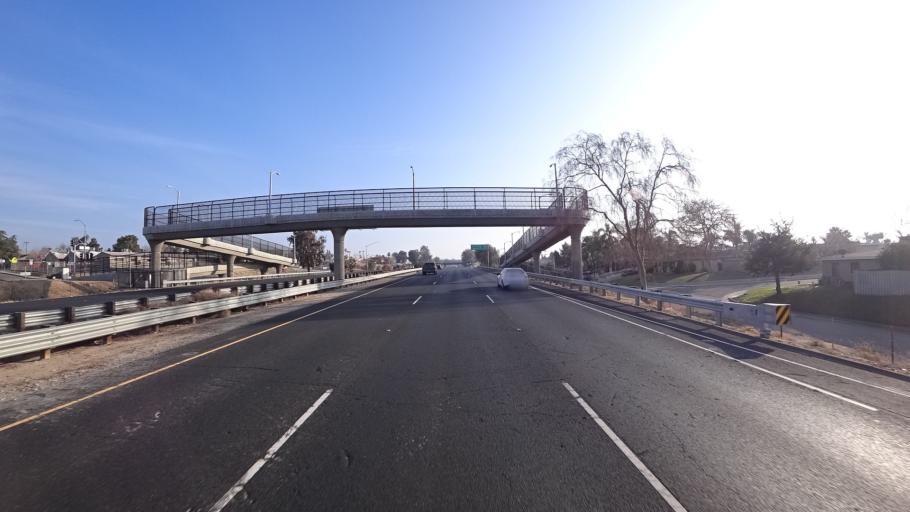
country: US
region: California
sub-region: Kern County
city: Bakersfield
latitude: 35.3932
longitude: -118.9721
